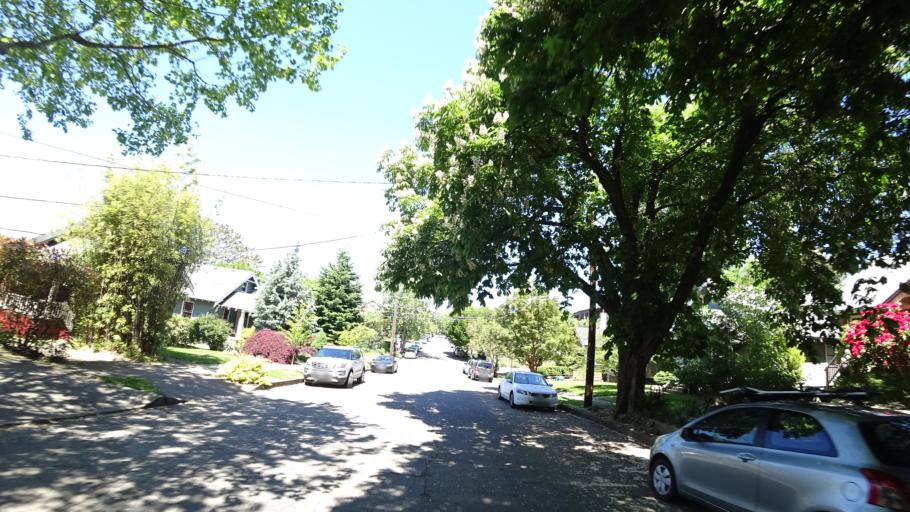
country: US
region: Oregon
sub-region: Multnomah County
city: Lents
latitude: 45.5029
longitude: -122.6121
